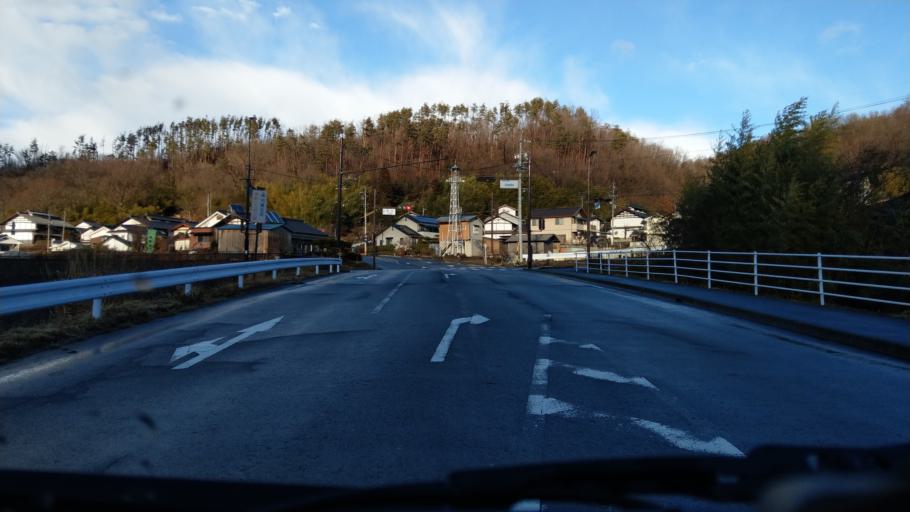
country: JP
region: Nagano
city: Kamimaruko
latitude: 36.2985
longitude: 138.3481
